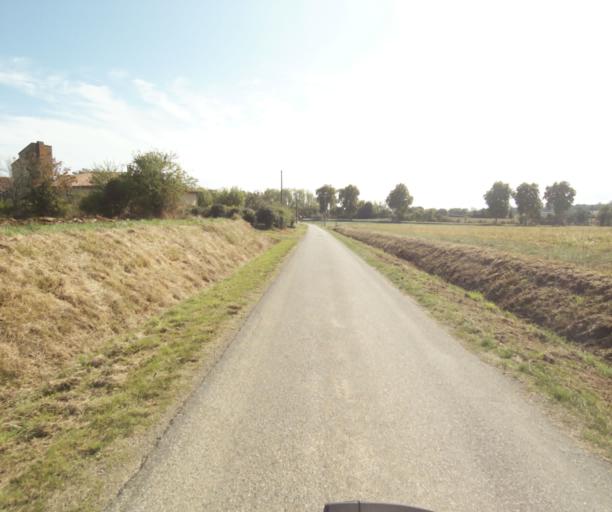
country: FR
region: Midi-Pyrenees
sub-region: Departement du Tarn-et-Garonne
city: Verdun-sur-Garonne
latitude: 43.8456
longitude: 1.1991
